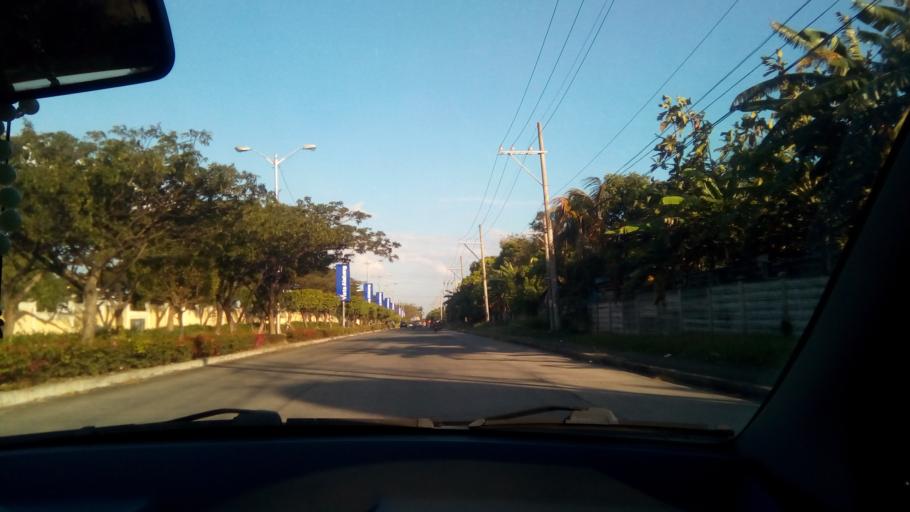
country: PH
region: Calabarzon
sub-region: Province of Laguna
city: San Pedro
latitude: 14.3805
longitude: 121.0134
